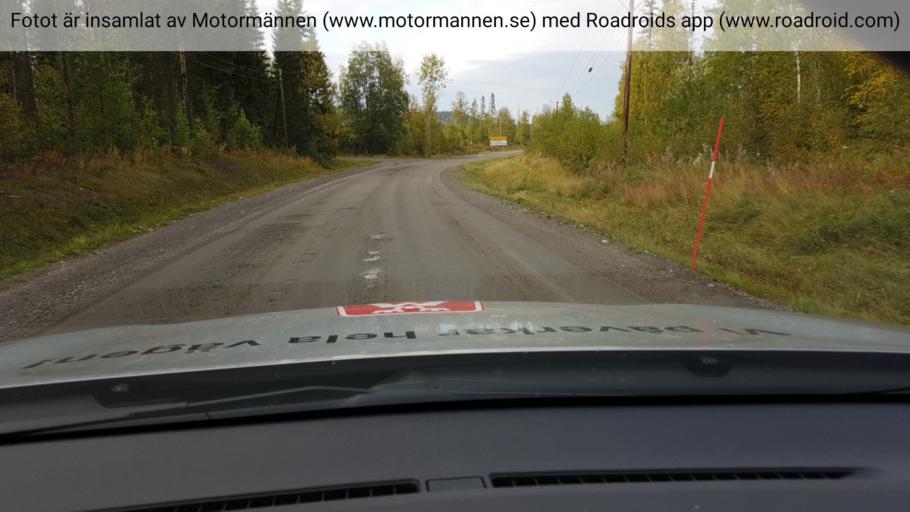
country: SE
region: Jaemtland
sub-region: Stroemsunds Kommun
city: Stroemsund
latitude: 63.9840
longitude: 15.8171
